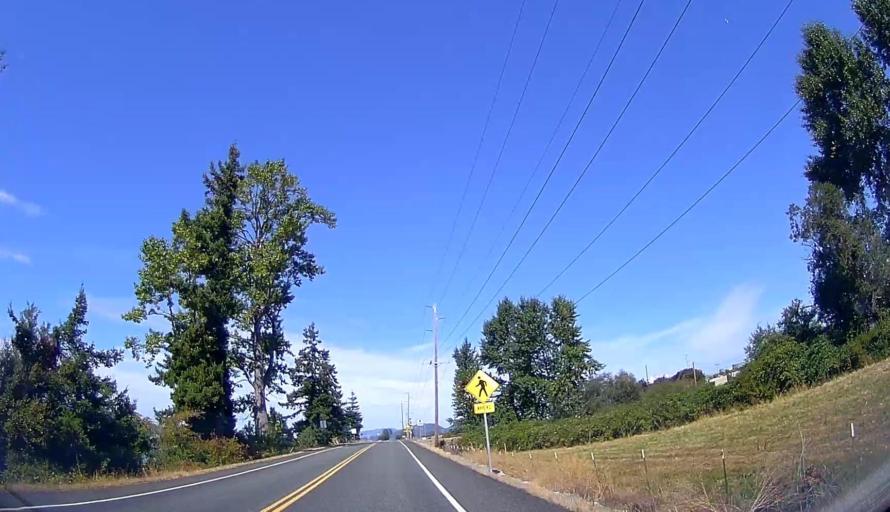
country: US
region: Washington
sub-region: Skagit County
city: Anacortes
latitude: 48.4758
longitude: -122.5721
